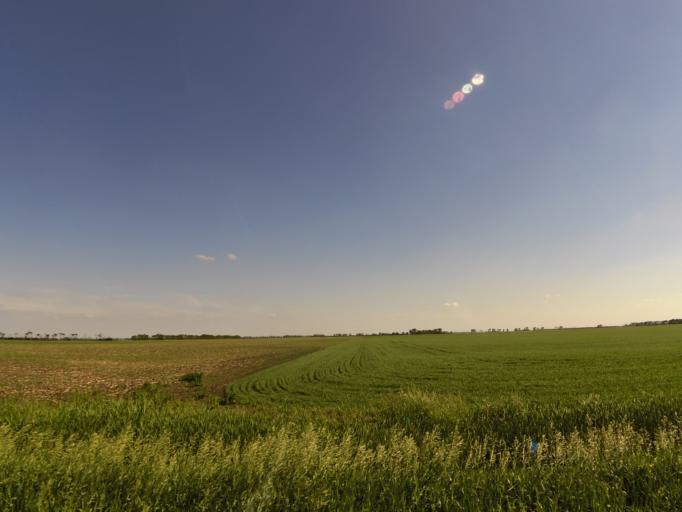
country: US
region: North Dakota
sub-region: Walsh County
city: Grafton
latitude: 48.3535
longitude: -97.2494
